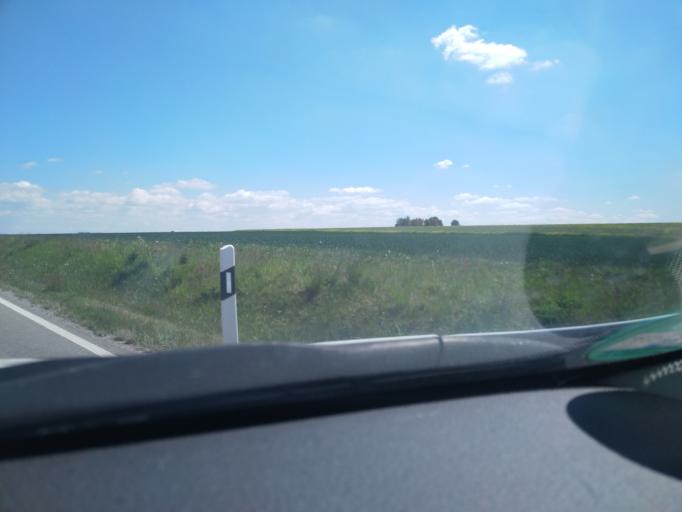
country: DE
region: Baden-Wuerttemberg
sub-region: Freiburg Region
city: Dunningen
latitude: 48.2152
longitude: 8.5265
